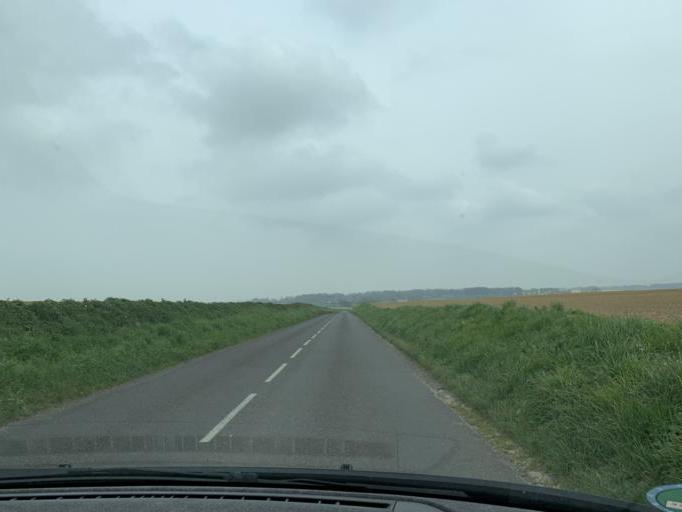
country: FR
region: Haute-Normandie
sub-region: Departement de la Seine-Maritime
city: Saint-Valery-en-Caux
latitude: 49.8552
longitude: 0.7681
